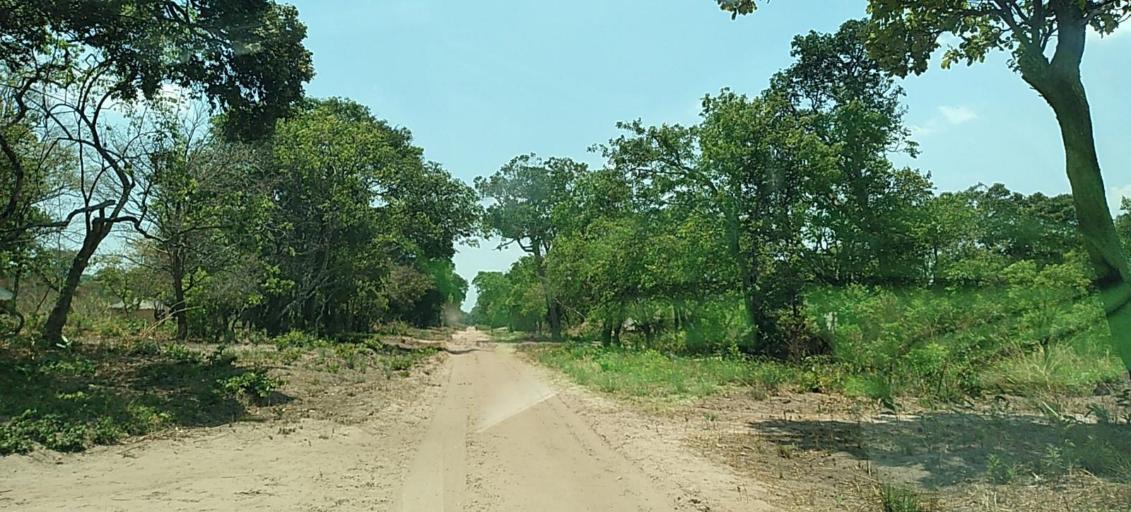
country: CD
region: Katanga
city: Kolwezi
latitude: -11.3702
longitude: 25.2122
